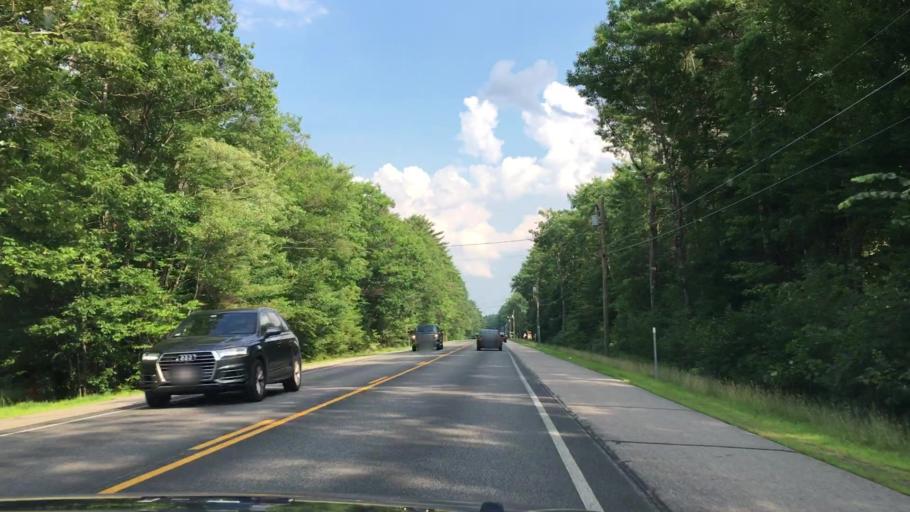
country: US
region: New Hampshire
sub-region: Strafford County
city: Farmington
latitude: 43.3960
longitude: -71.0999
